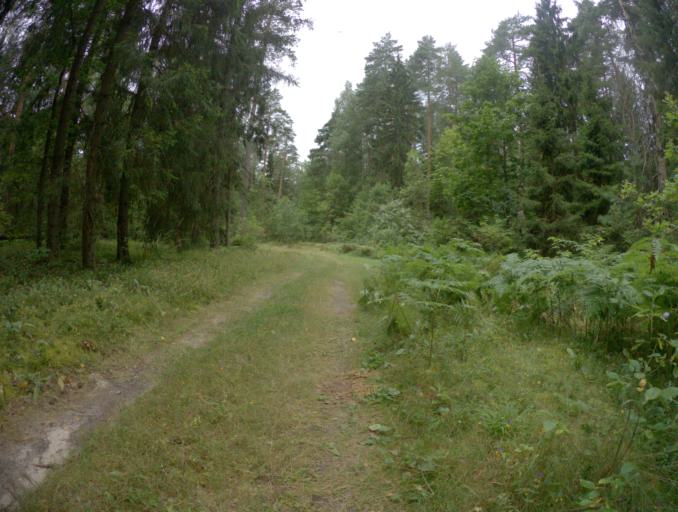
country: RU
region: Vladimir
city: Bogolyubovo
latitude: 56.1395
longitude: 40.5516
